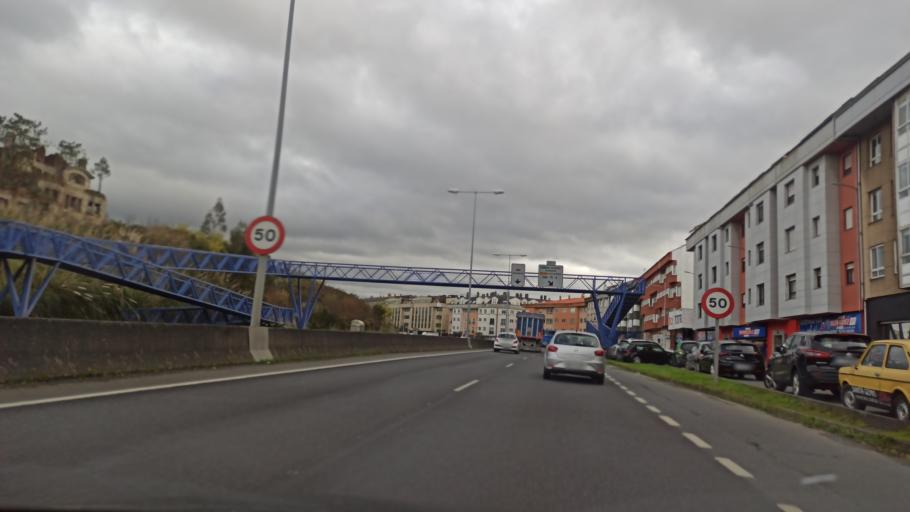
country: ES
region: Galicia
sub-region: Provincia da Coruna
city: Cambre
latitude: 43.3222
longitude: -8.3597
